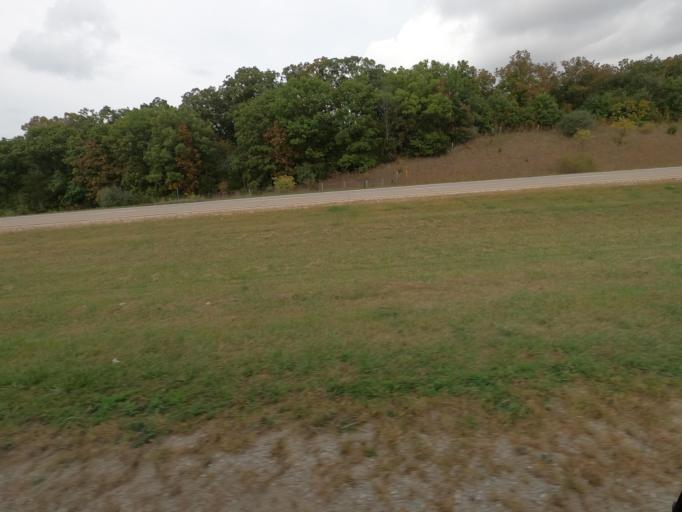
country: US
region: Iowa
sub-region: Wapello County
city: Ottumwa
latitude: 40.9989
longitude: -92.3397
